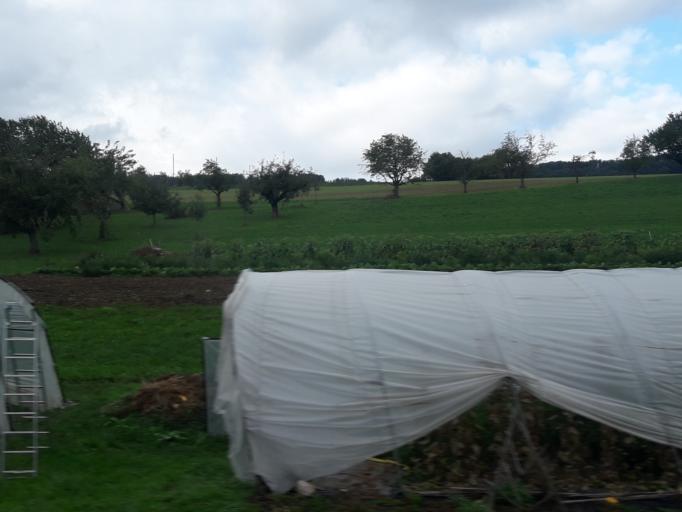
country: CH
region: Bern
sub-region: Bern-Mittelland District
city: Muhlethurnen
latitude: 46.8320
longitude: 7.5063
